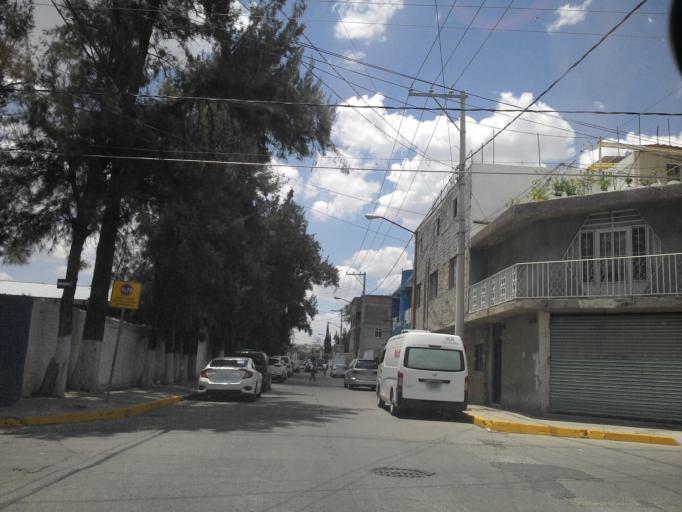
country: MX
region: Guanajuato
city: San Francisco del Rincon
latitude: 21.0254
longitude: -101.8574
